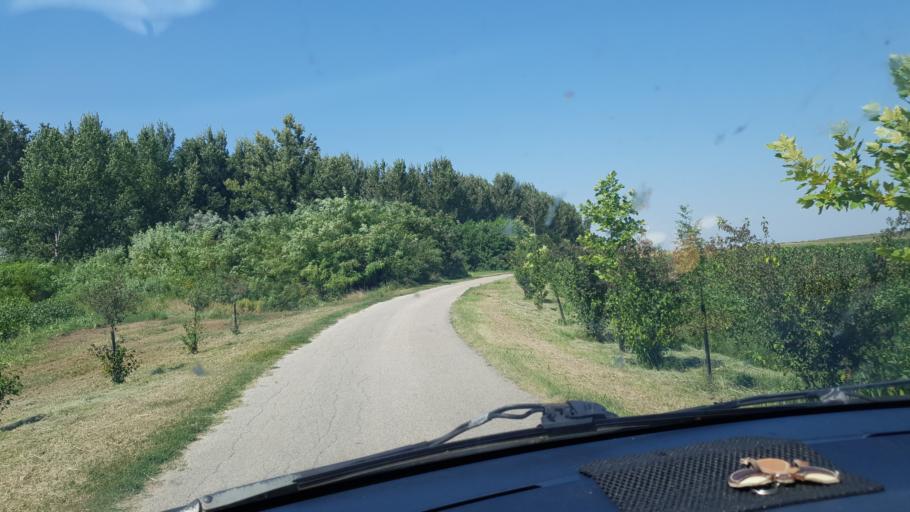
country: RS
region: Autonomna Pokrajina Vojvodina
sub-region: Juznobacki Okrug
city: Kovilj
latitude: 45.2014
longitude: 20.0631
